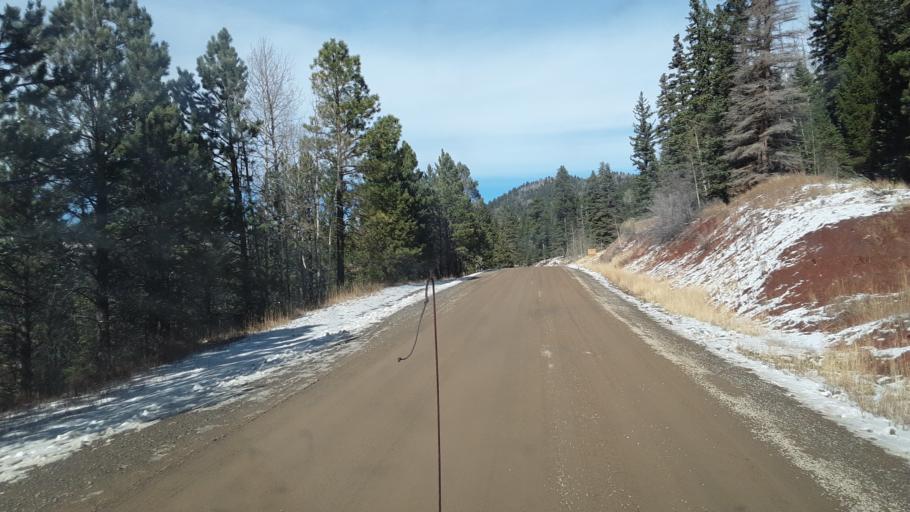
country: US
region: Colorado
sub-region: La Plata County
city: Bayfield
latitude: 37.4018
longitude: -107.6594
